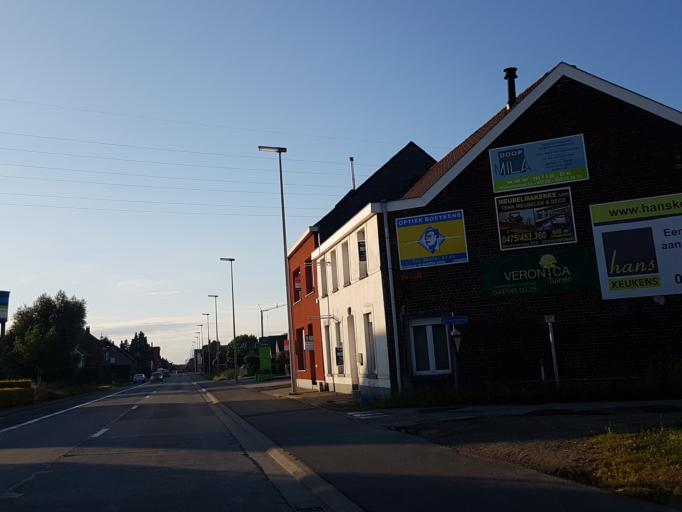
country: BE
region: Flanders
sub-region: Provincie Oost-Vlaanderen
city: Lebbeke
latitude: 50.9891
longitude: 4.1360
